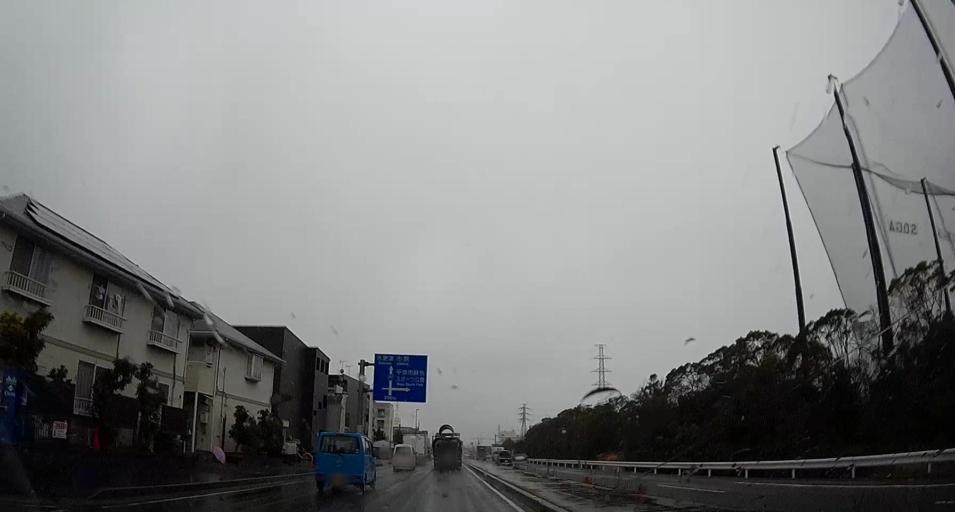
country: JP
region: Chiba
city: Chiba
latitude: 35.5752
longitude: 140.1281
